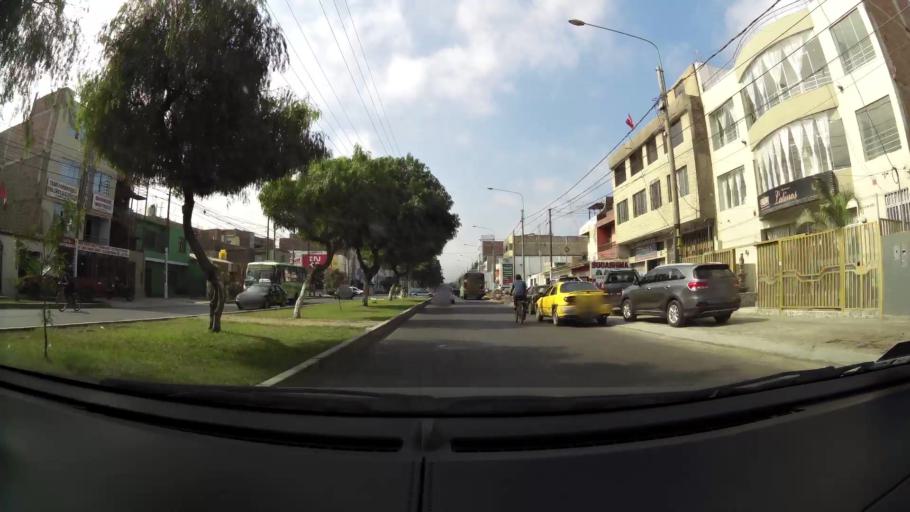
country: PE
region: La Libertad
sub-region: Provincia de Trujillo
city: Trujillo
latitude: -8.1096
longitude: -79.0125
